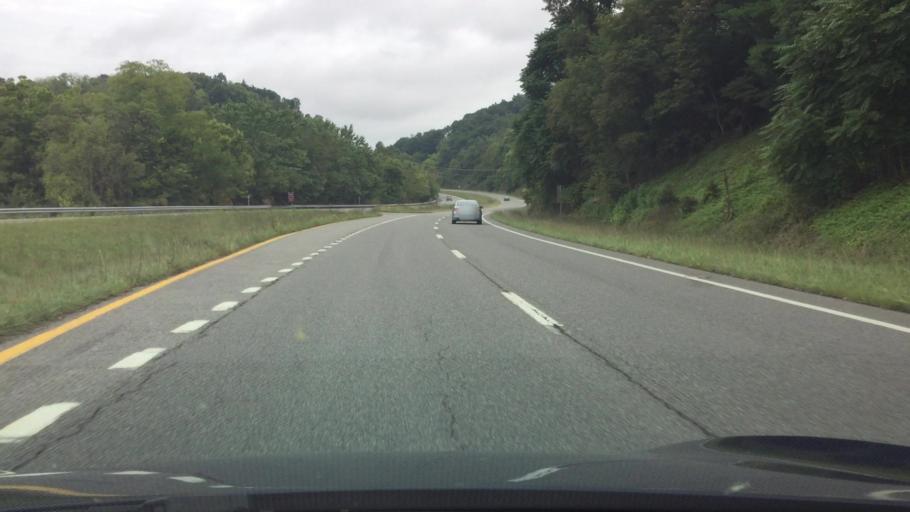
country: US
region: Virginia
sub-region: City of Radford
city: Radford
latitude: 37.1057
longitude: -80.5198
